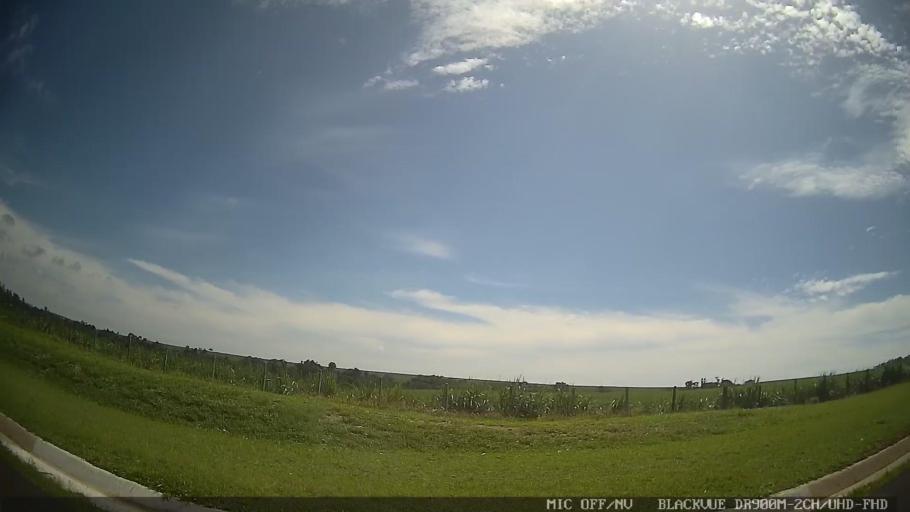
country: BR
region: Sao Paulo
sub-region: Tiete
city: Tiete
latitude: -23.1488
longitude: -47.6662
